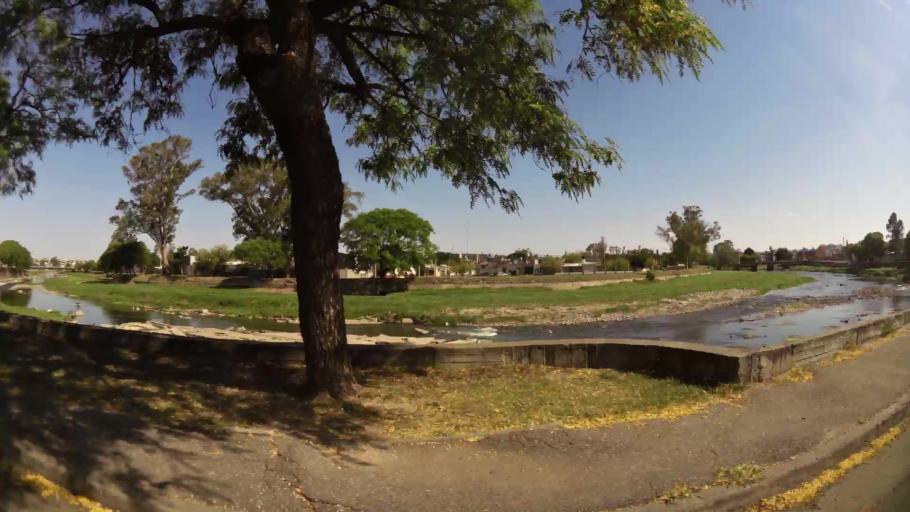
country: AR
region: Cordoba
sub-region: Departamento de Capital
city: Cordoba
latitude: -31.4159
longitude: -64.1564
